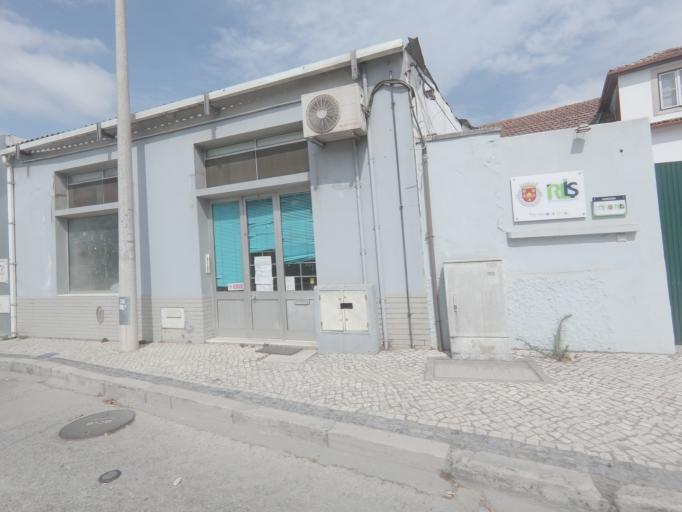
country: PT
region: Leiria
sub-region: Leiria
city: Leiria
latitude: 39.7422
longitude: -8.8112
